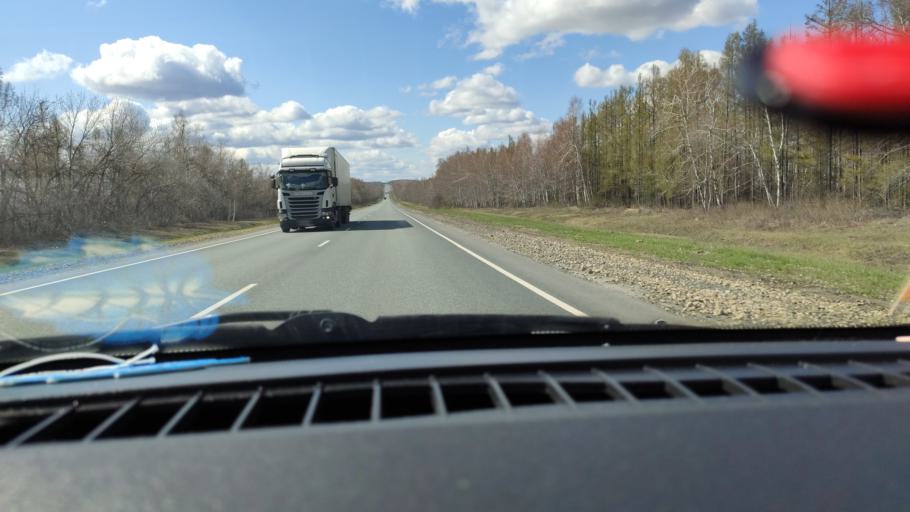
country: RU
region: Saratov
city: Khvalynsk
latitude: 52.5775
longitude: 48.1117
